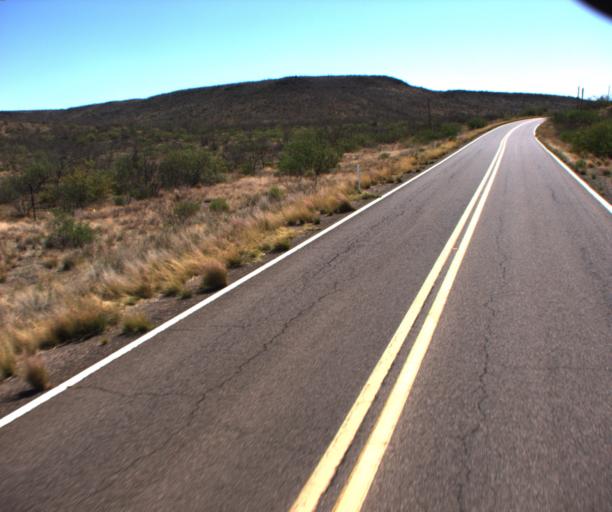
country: US
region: Arizona
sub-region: Cochise County
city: Douglas
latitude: 31.4736
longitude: -109.3923
